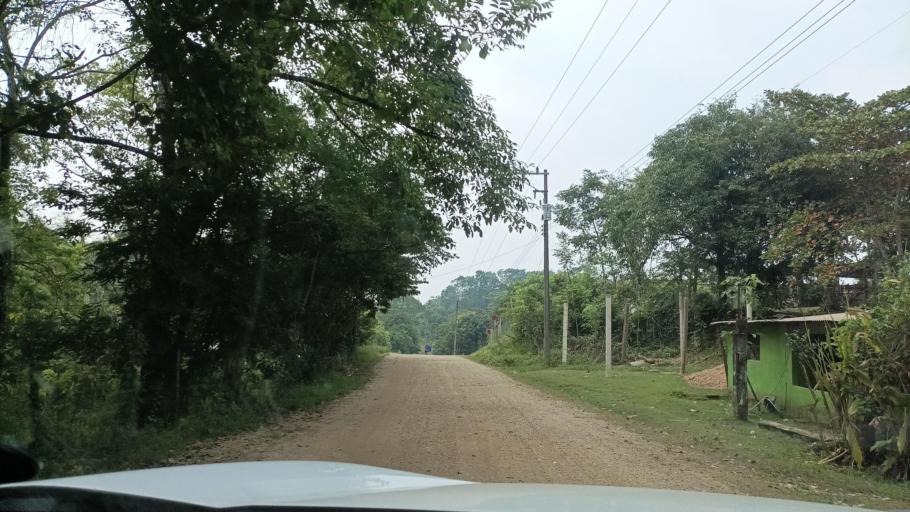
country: MX
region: Veracruz
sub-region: Moloacan
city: Cuichapa
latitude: 17.5799
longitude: -94.2324
